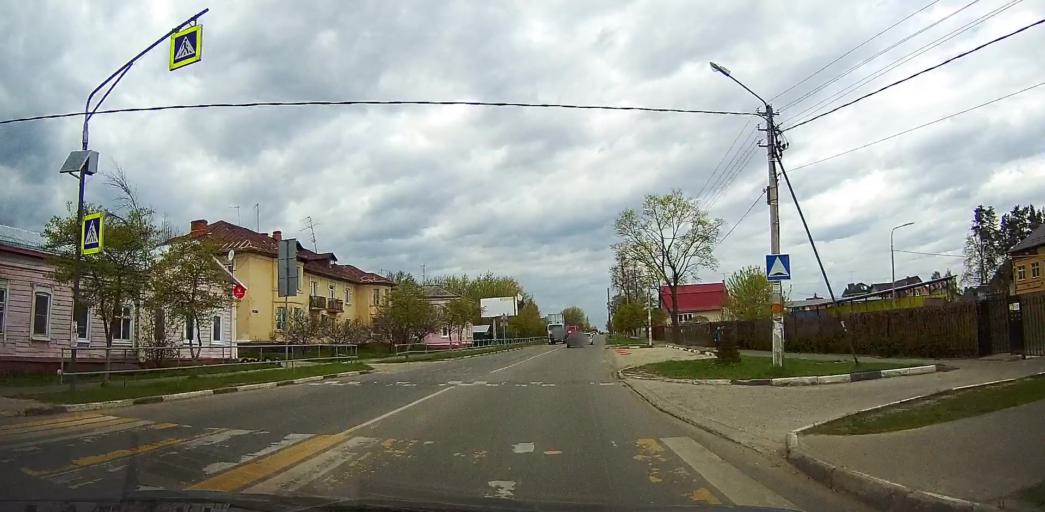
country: RU
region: Moskovskaya
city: Pavlovskiy Posad
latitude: 55.7856
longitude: 38.6481
